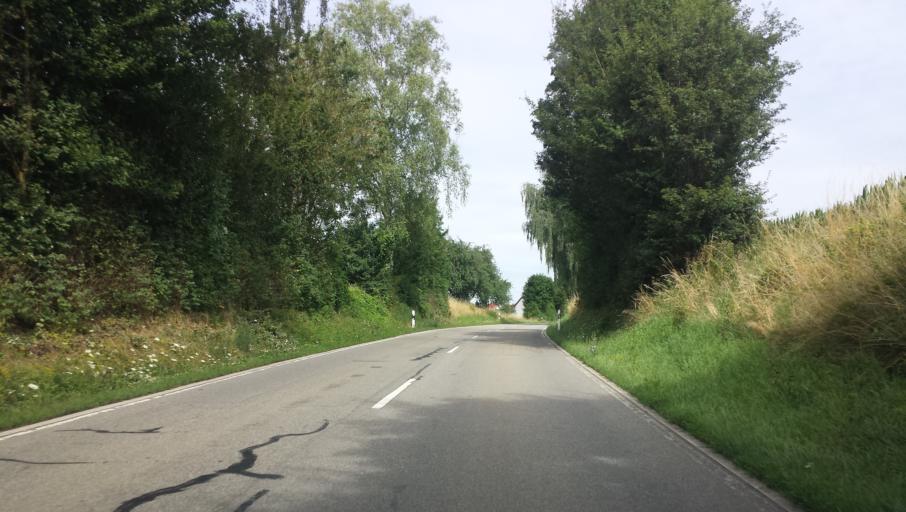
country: DE
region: Baden-Wuerttemberg
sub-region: Karlsruhe Region
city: Neidenstein
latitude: 49.2882
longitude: 8.8812
